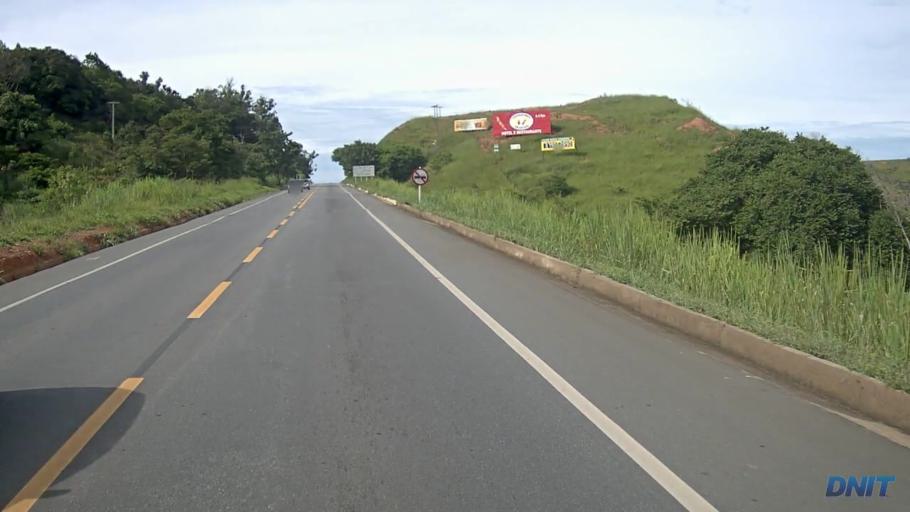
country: BR
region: Minas Gerais
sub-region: Belo Oriente
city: Belo Oriente
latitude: -19.2533
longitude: -42.3405
